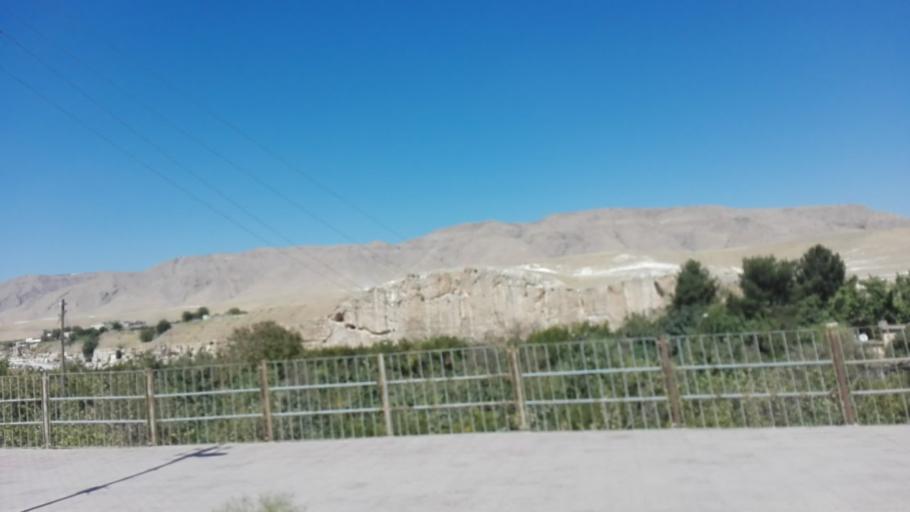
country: TR
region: Batman
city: Hasankeyf
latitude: 37.7132
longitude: 41.4204
